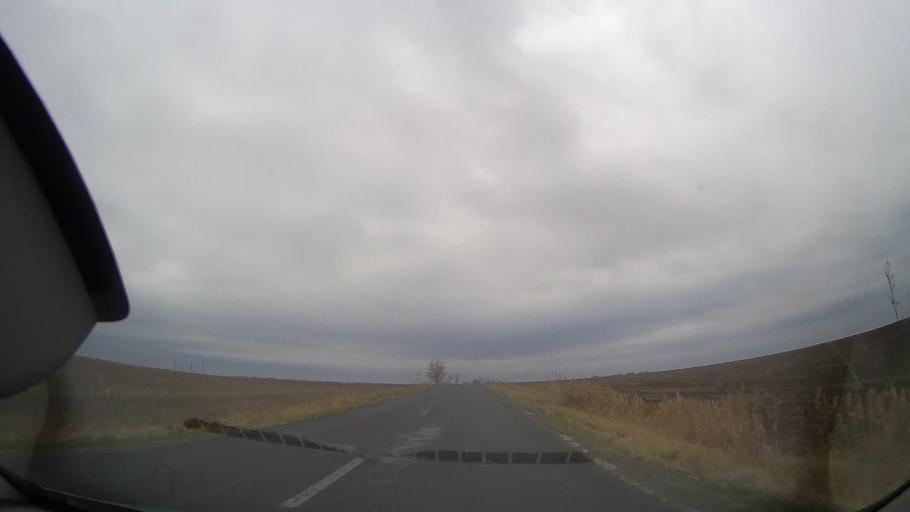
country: RO
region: Buzau
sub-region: Comuna Padina
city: Padina
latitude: 44.8003
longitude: 27.1357
